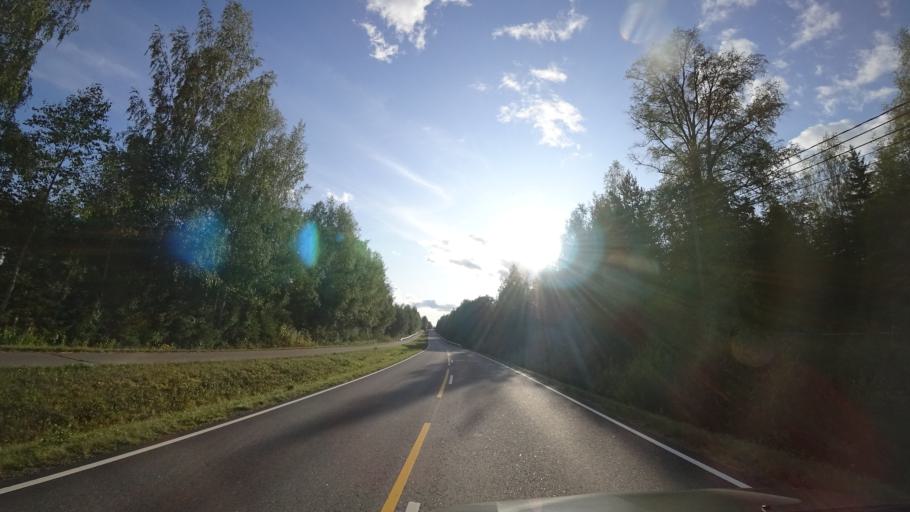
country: FI
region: Paijanne Tavastia
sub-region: Lahti
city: Haemeenkoski
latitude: 61.0775
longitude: 25.1029
